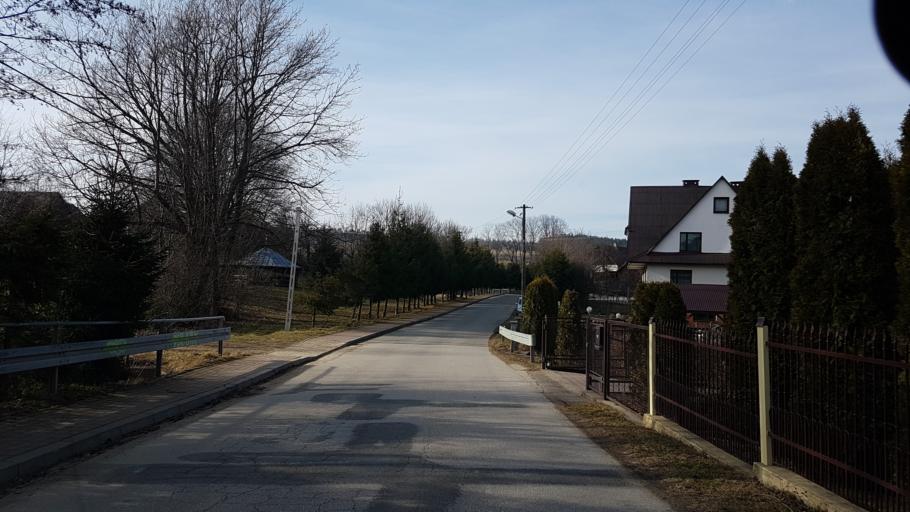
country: PL
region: Lesser Poland Voivodeship
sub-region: Powiat nowosadecki
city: Stary Sacz
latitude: 49.5453
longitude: 20.6270
